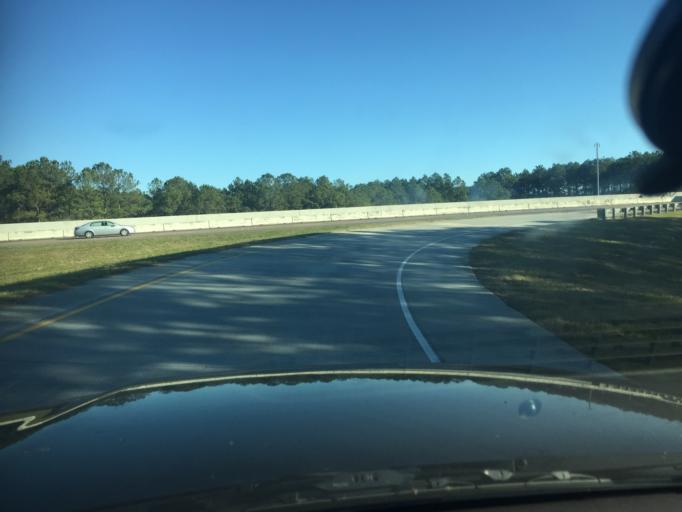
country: US
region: Louisiana
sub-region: Saint Tammany Parish
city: Slidell
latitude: 30.3063
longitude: -89.7431
